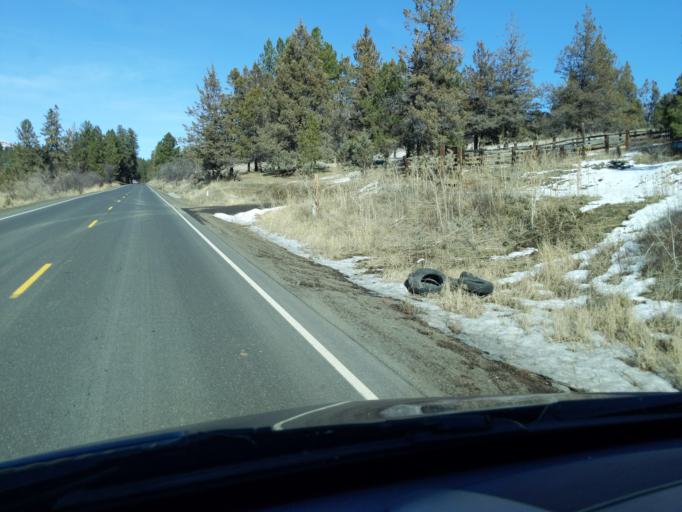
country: US
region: Oregon
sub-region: Grant County
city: John Day
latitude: 44.8652
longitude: -119.0248
